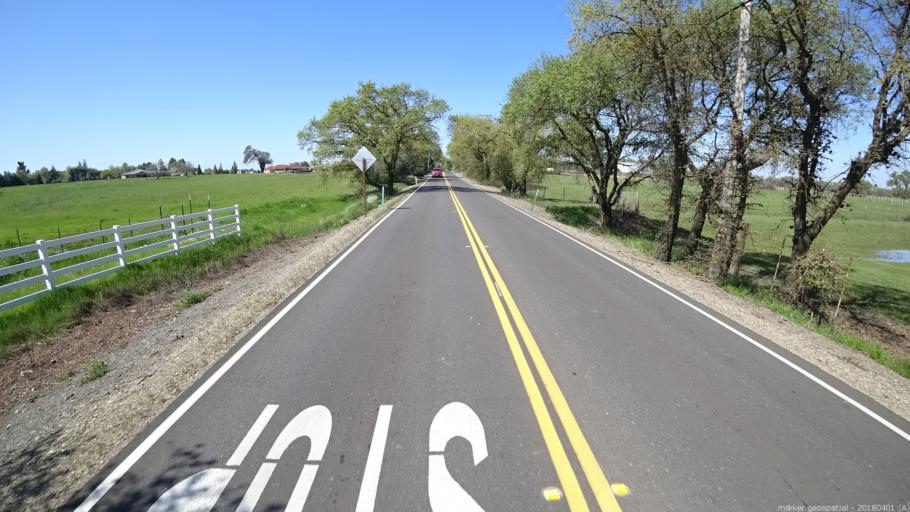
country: US
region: California
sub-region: Sacramento County
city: Wilton
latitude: 38.4118
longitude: -121.2650
